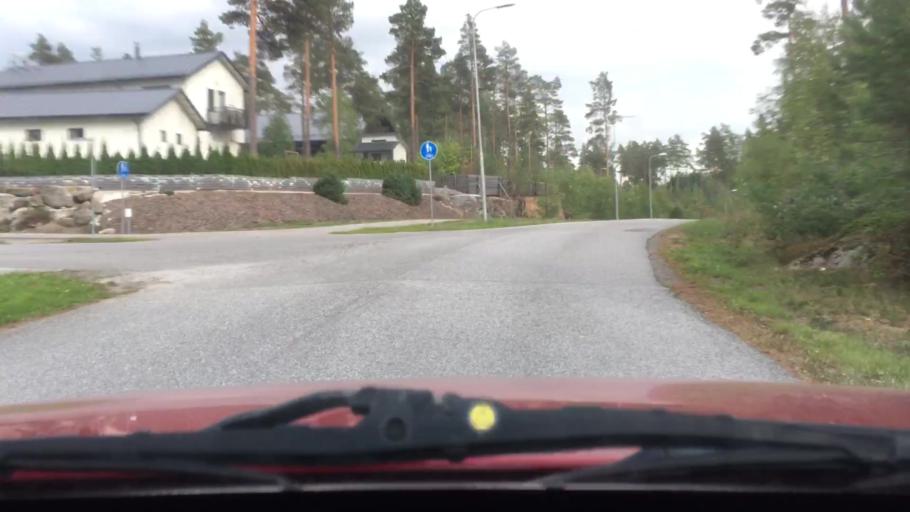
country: FI
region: Varsinais-Suomi
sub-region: Turku
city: Masku
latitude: 60.5594
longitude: 22.1391
